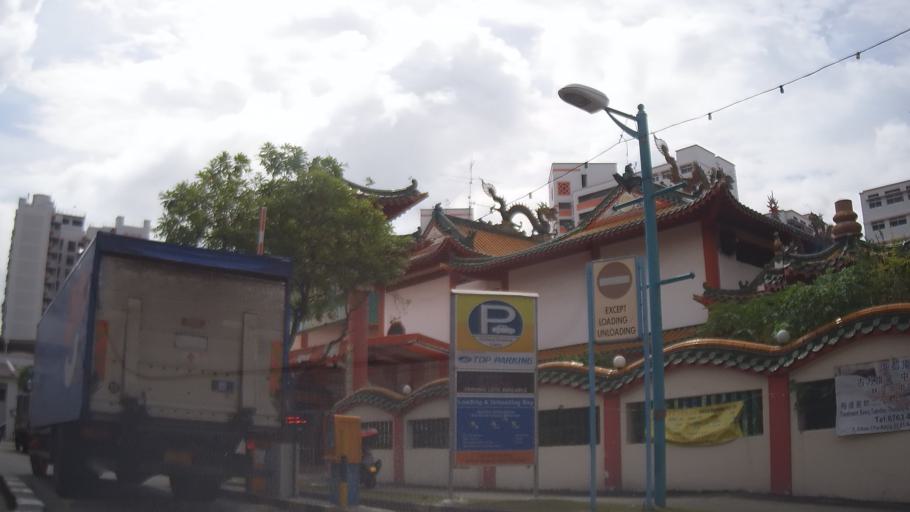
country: MY
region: Johor
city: Johor Bahru
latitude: 1.3922
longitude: 103.7425
